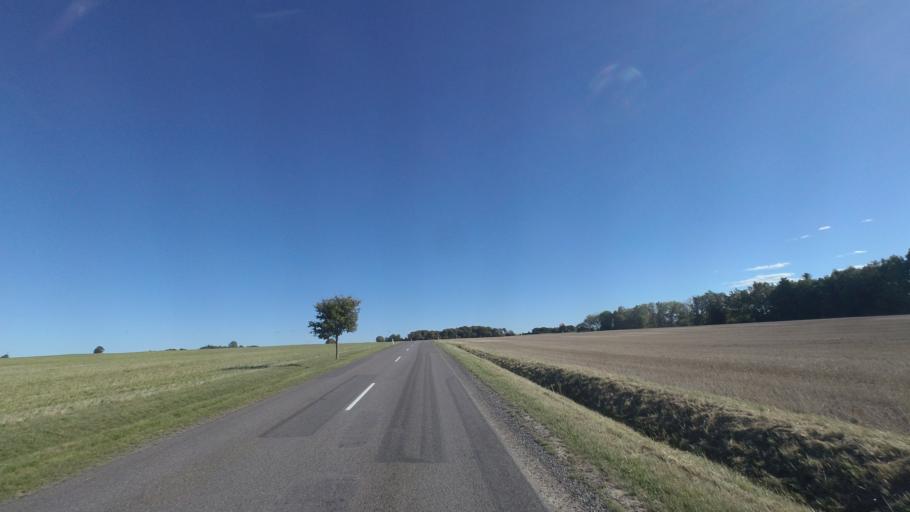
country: DK
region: Capital Region
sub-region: Bornholm Kommune
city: Nexo
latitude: 55.1229
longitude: 15.0941
